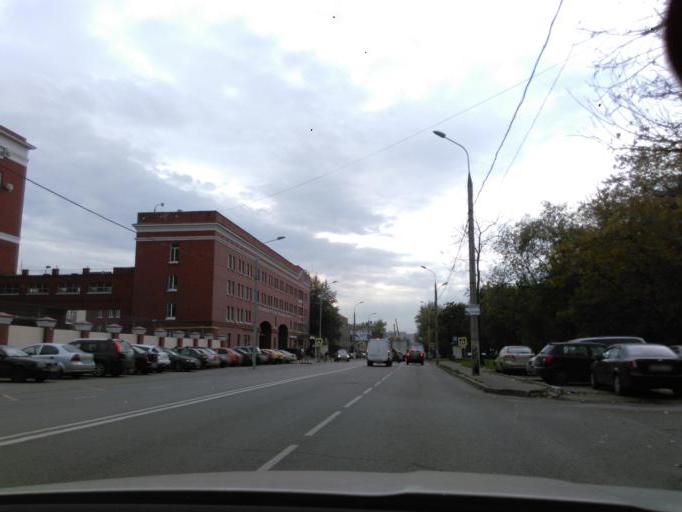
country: RU
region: Moscow
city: Ostankinskiy
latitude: 55.8167
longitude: 37.5974
